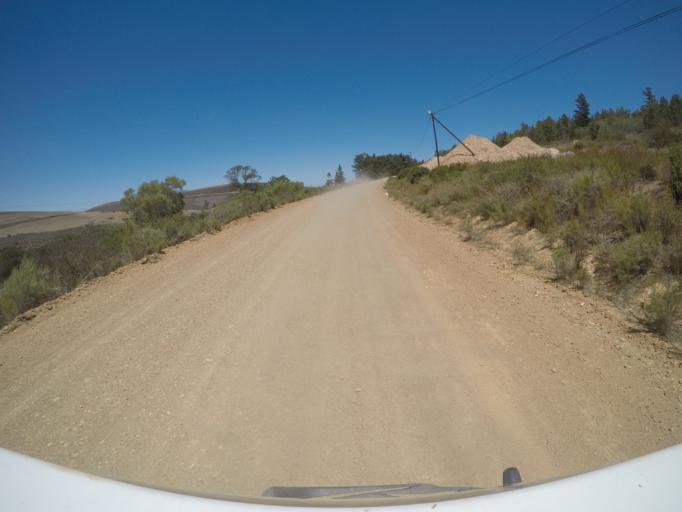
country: ZA
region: Western Cape
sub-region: Overberg District Municipality
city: Caledon
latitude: -34.1724
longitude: 19.2290
